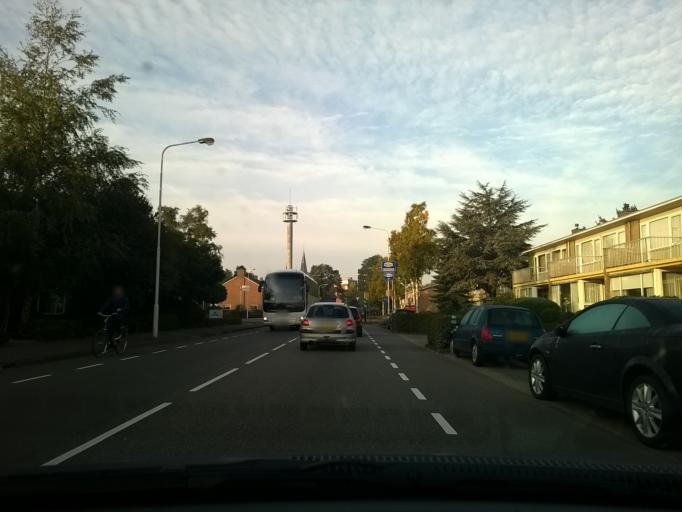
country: NL
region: Friesland
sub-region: Gemeente Heerenveen
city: Heerenveen
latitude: 52.9631
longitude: 5.9254
